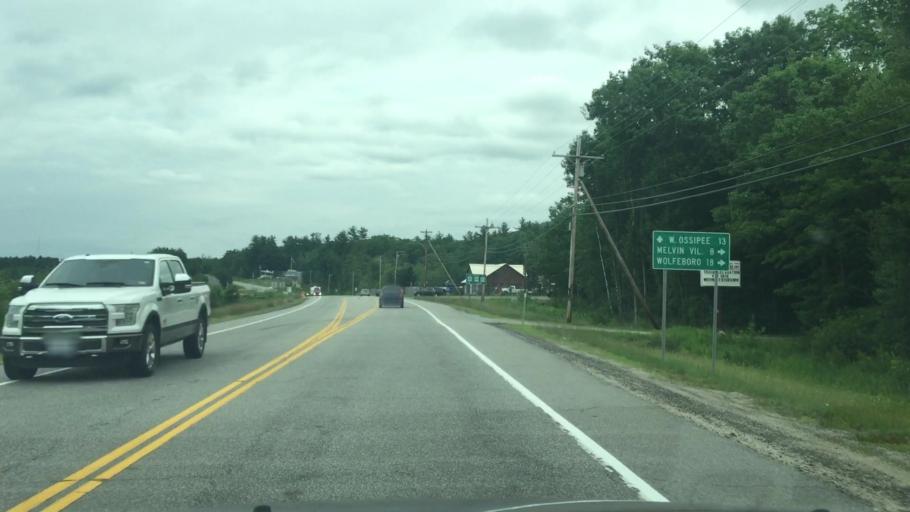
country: US
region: New Hampshire
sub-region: Carroll County
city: Moultonborough
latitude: 43.7603
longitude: -71.3892
